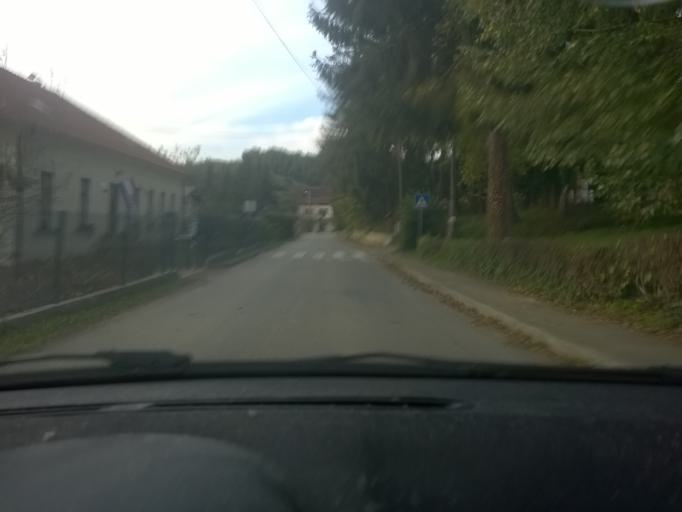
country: HR
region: Krapinsko-Zagorska
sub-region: Grad Krapina
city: Krapina
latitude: 46.1256
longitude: 15.8504
